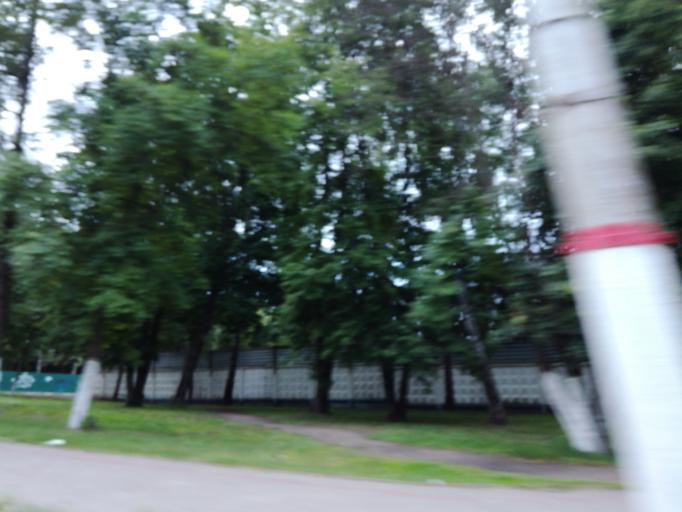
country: RU
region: Kursk
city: Kursk
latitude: 51.7643
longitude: 36.1773
